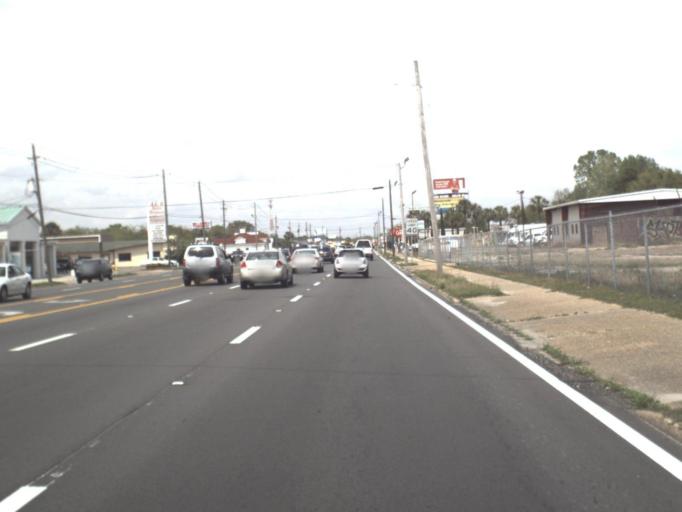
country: US
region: Florida
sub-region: Okaloosa County
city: Ocean City
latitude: 30.4352
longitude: -86.6026
